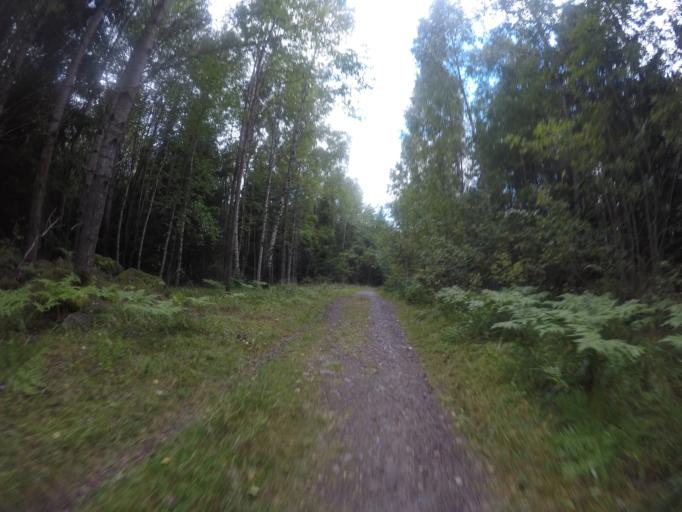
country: SE
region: Vaestmanland
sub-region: Vasteras
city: Vasteras
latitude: 59.6609
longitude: 16.5322
